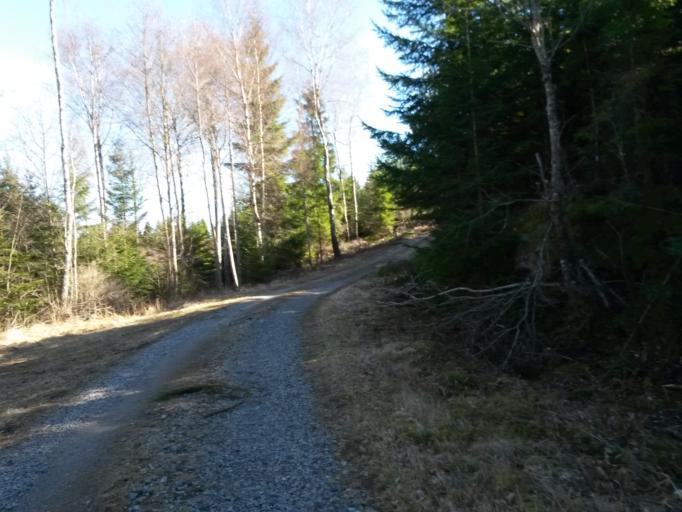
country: SE
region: Vaestra Goetaland
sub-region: Vargarda Kommun
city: Jonstorp
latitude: 57.9679
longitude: 12.6759
